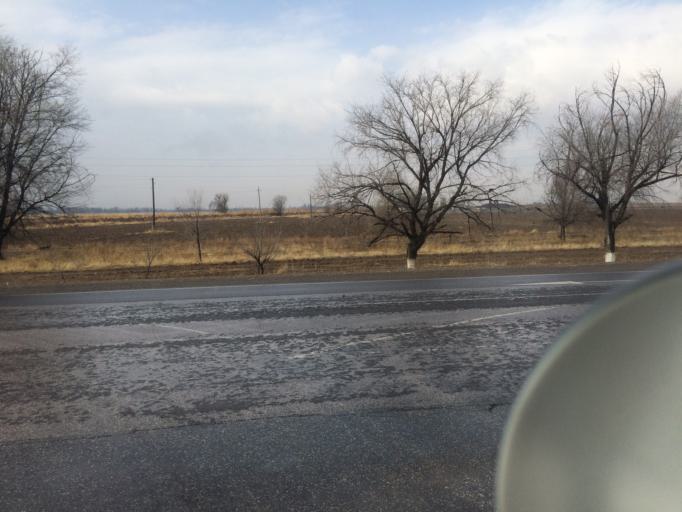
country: KZ
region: Zhambyl
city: Georgiyevka
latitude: 43.0889
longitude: 74.7055
